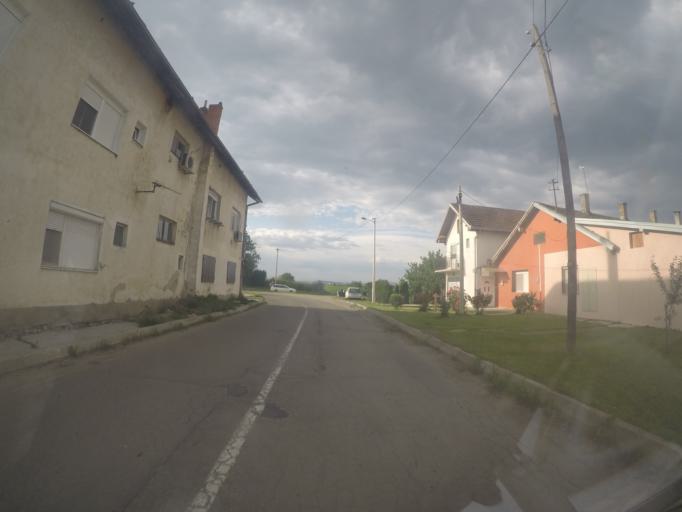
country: RS
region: Central Serbia
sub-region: Belgrade
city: Zemun
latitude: 44.9088
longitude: 20.4308
